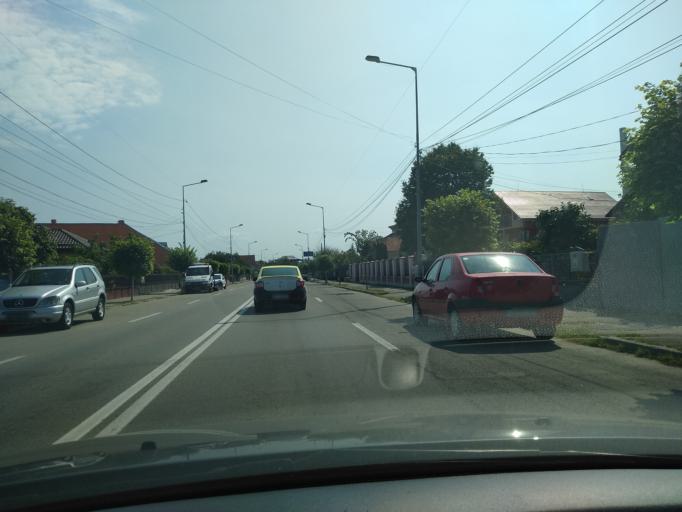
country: RO
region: Gorj
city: Targu Jiu
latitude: 45.0203
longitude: 23.2683
